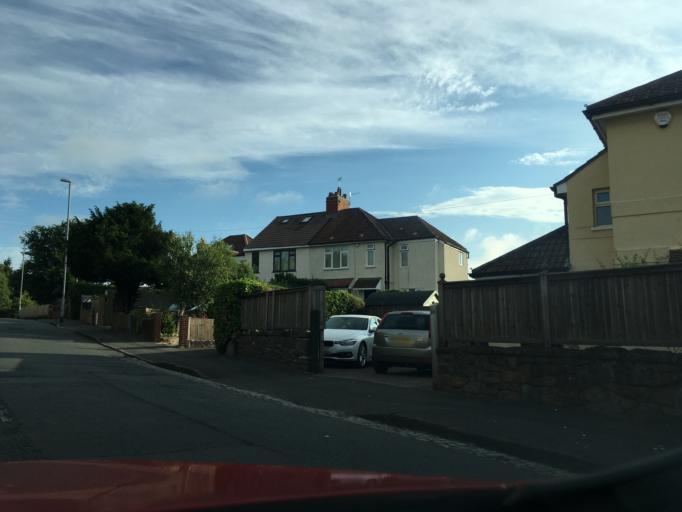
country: GB
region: England
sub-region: Bristol
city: Bristol
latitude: 51.4912
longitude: -2.6371
